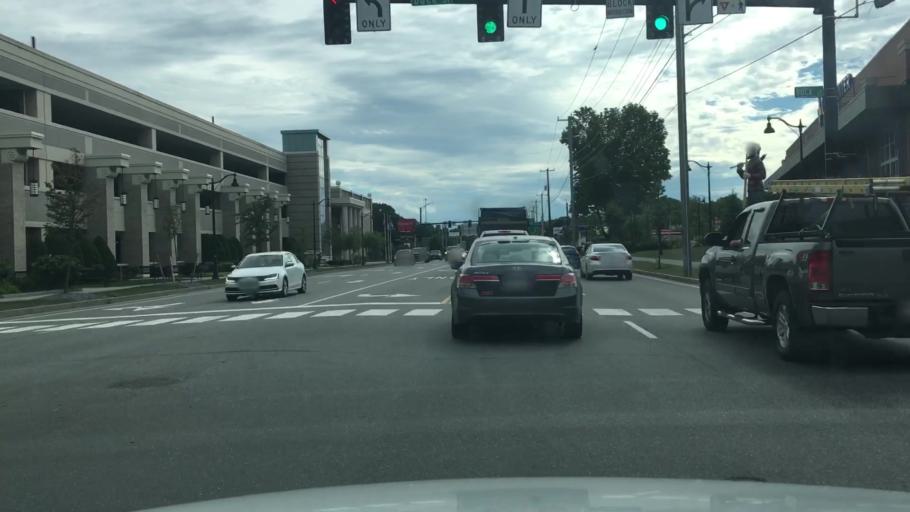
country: US
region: Maine
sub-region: Penobscot County
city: Bangor
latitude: 44.7895
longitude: -68.7775
